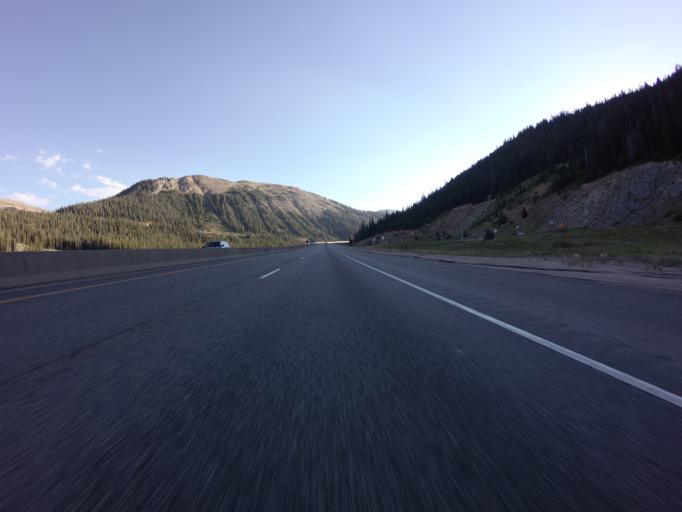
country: US
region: Colorado
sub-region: Summit County
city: Keystone
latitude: 39.6862
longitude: -105.8847
